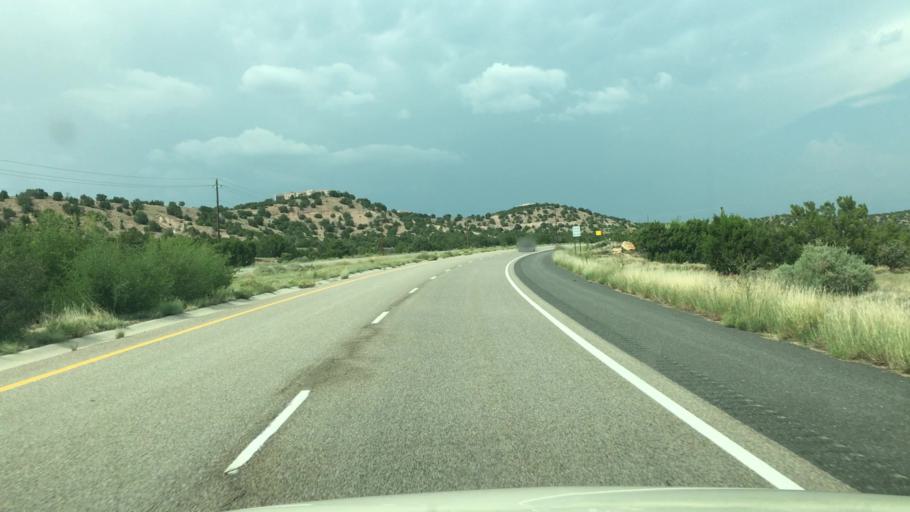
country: US
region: New Mexico
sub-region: Santa Fe County
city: Eldorado at Santa Fe
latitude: 35.4816
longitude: -105.9081
